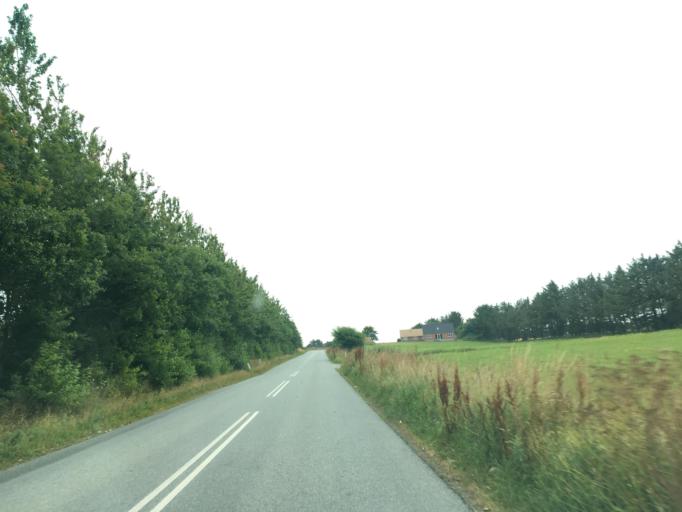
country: DK
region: North Denmark
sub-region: Thisted Kommune
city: Hurup
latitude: 56.7974
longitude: 8.4121
